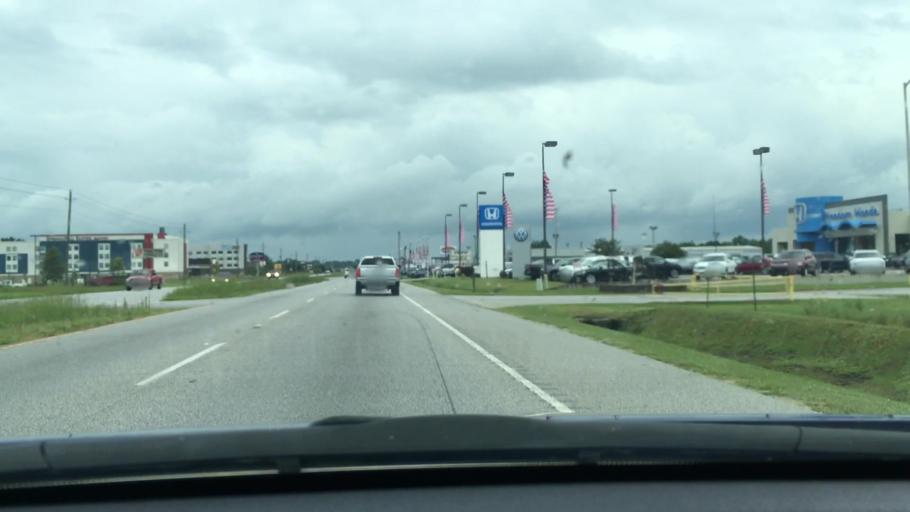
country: US
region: South Carolina
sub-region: Sumter County
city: Cherryvale
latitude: 33.9632
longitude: -80.4032
